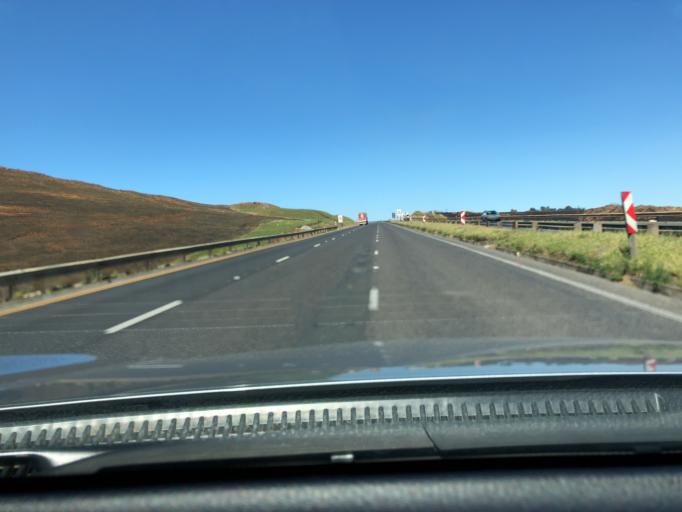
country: ZA
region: KwaZulu-Natal
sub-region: uMgungundlovu District Municipality
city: Howick
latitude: -29.4319
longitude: 30.1716
